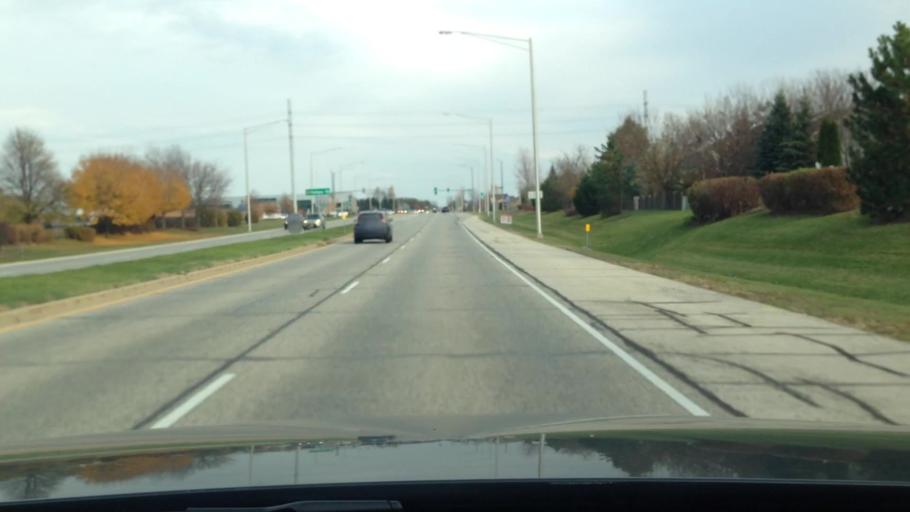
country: US
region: Illinois
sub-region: McHenry County
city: Huntley
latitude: 42.1755
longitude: -88.4063
